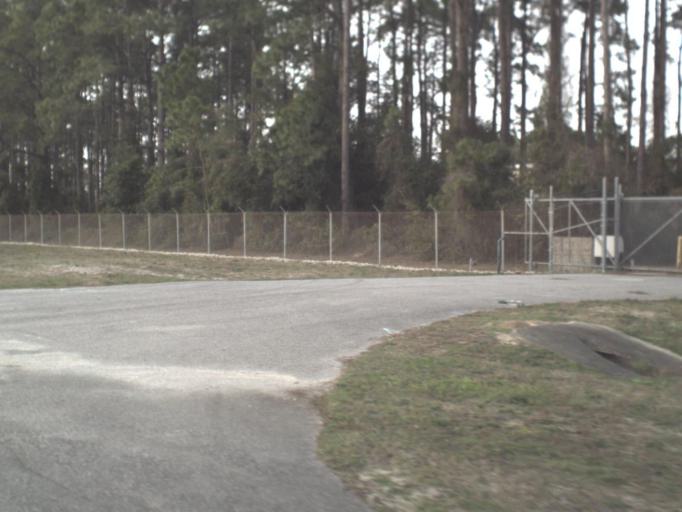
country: US
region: Florida
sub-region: Bay County
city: Tyndall Air Force Base
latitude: 30.0592
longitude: -85.5762
